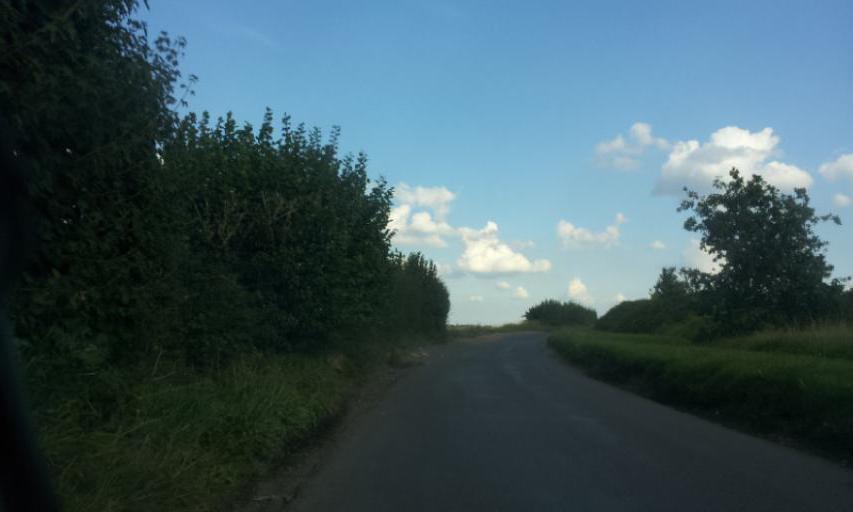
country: GB
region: England
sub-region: Kent
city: Eynsford
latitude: 51.4044
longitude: 0.2167
